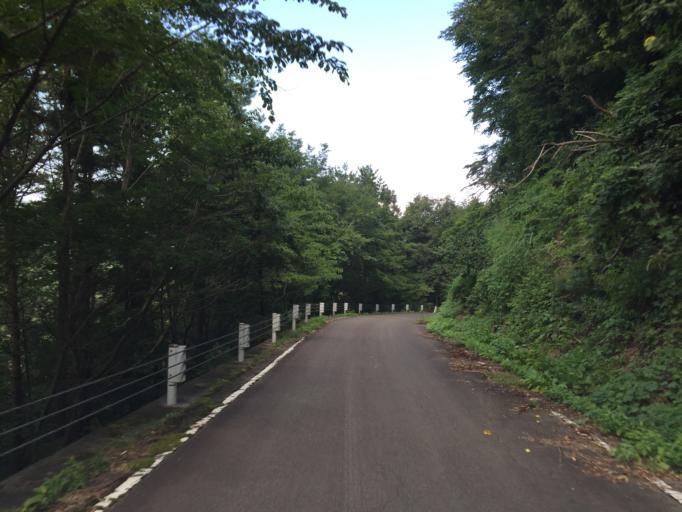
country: JP
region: Fukushima
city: Inawashiro
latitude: 37.4257
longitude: 140.0564
